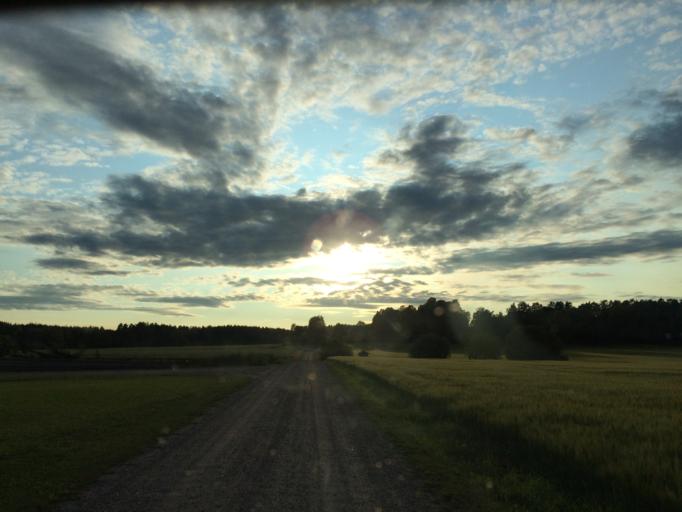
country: FI
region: Haeme
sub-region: Haemeenlinna
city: Janakkala
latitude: 60.8864
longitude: 24.6273
